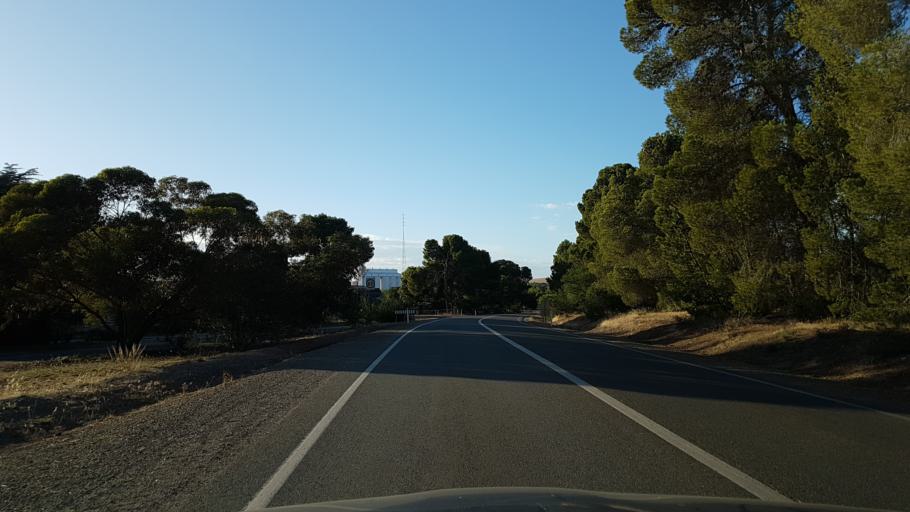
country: AU
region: South Australia
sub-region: Port Pirie City and Dists
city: Crystal Brook
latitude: -33.2697
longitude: 138.3513
